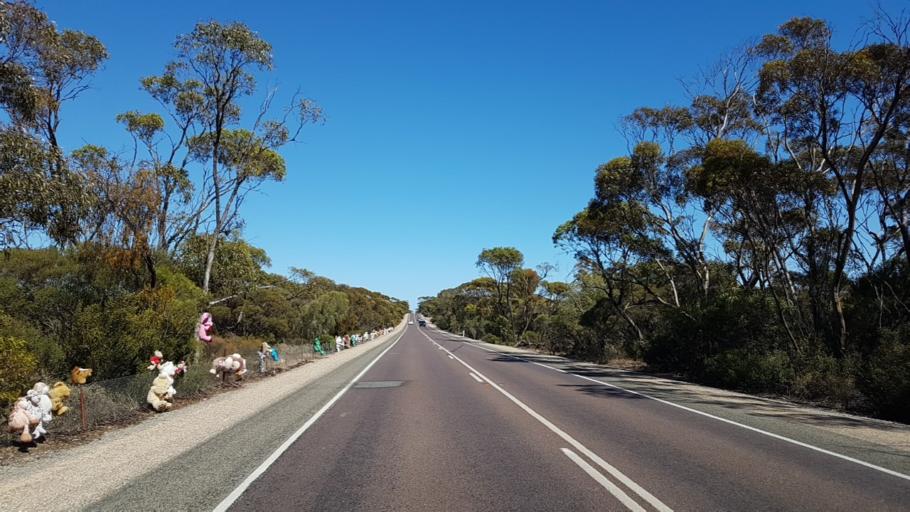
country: AU
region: South Australia
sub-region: Copper Coast
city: Kadina
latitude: -34.0489
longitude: 137.9695
